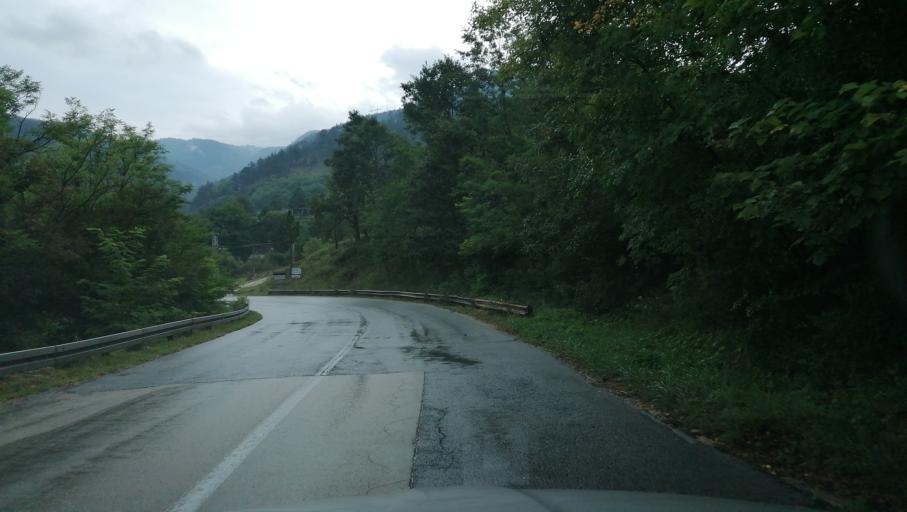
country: RS
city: Durici
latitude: 43.8018
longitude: 19.5062
